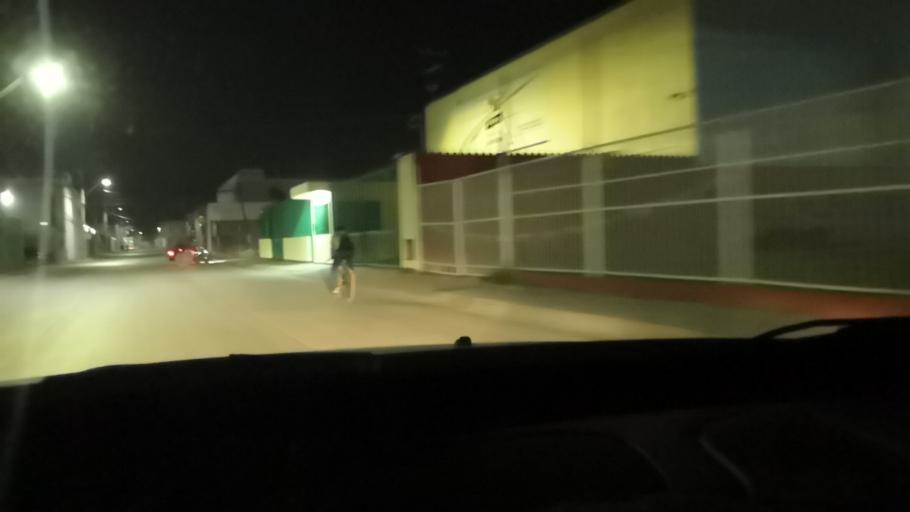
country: MX
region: Guanajuato
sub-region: Leon
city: Fraccionamiento Paraiso Real
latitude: 21.0852
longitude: -101.6231
